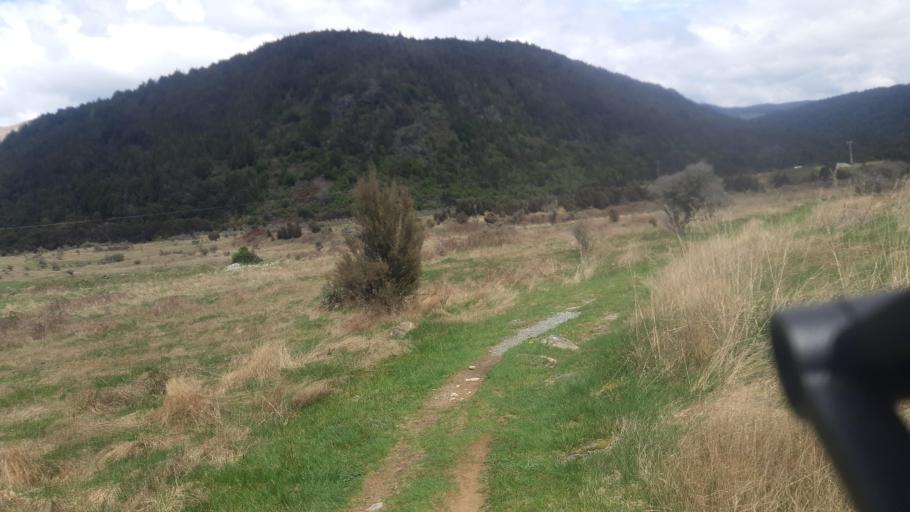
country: NZ
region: Tasman
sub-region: Tasman District
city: Wakefield
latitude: -41.7935
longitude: 172.8389
